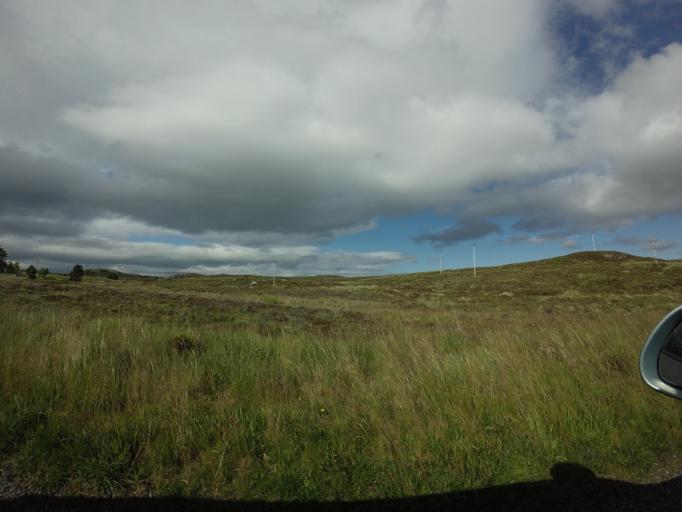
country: GB
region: Scotland
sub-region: Eilean Siar
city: Harris
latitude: 58.1922
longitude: -6.7098
